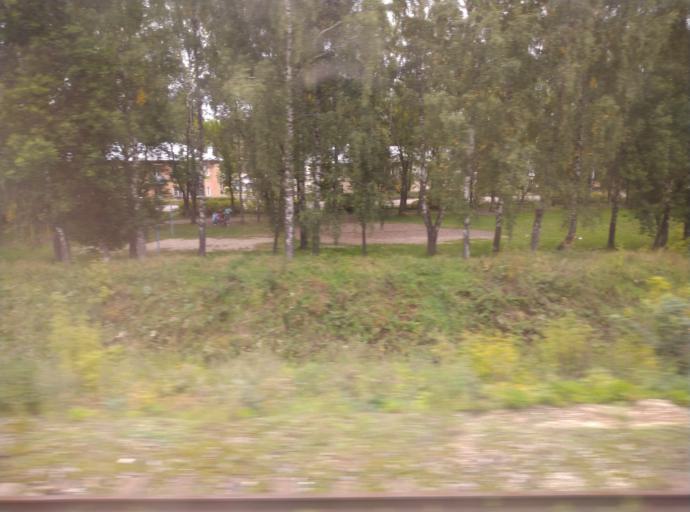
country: RU
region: Kostroma
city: Nerekhta
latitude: 57.4647
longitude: 40.5557
